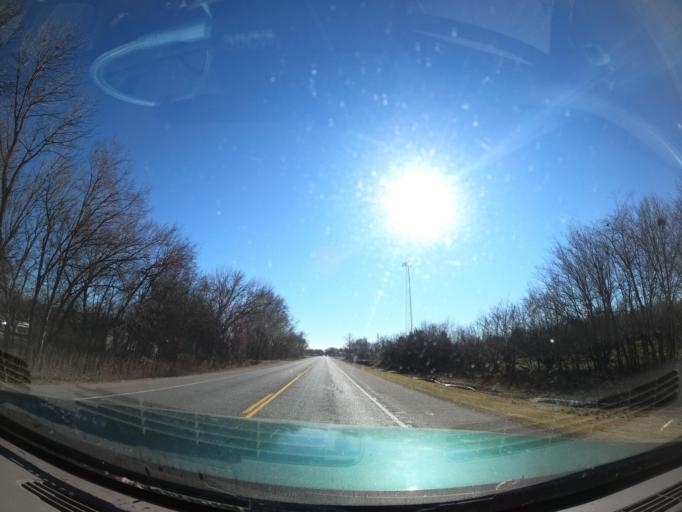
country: US
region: Oklahoma
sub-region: Muskogee County
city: Haskell
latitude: 35.8271
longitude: -95.6775
